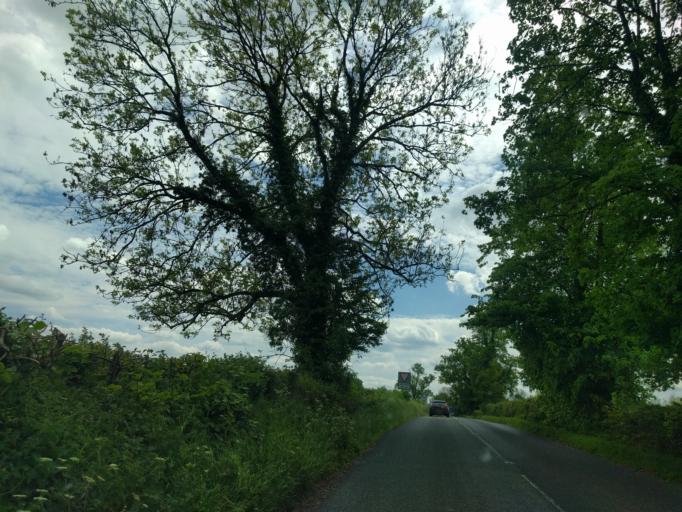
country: GB
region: England
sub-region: Wiltshire
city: Chippenham
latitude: 51.5045
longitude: -2.0981
